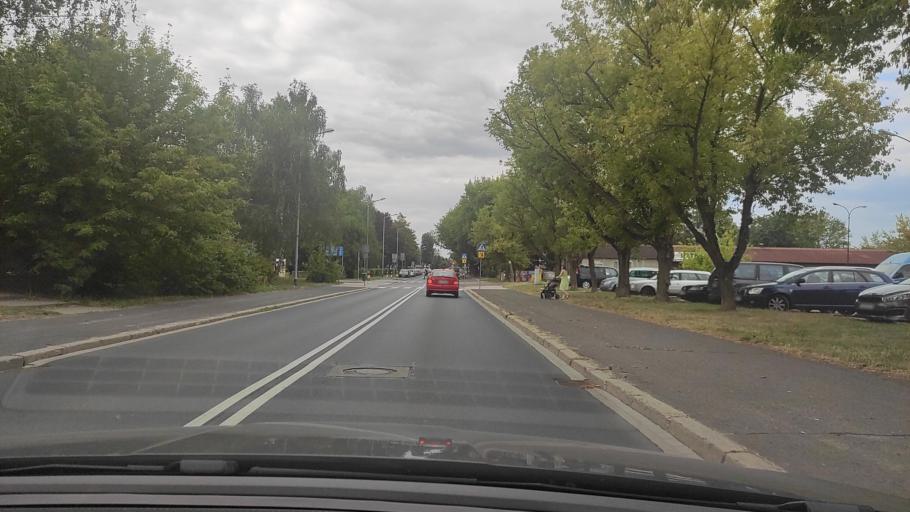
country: PL
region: Greater Poland Voivodeship
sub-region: Powiat poznanski
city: Swarzedz
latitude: 52.4191
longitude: 17.0818
